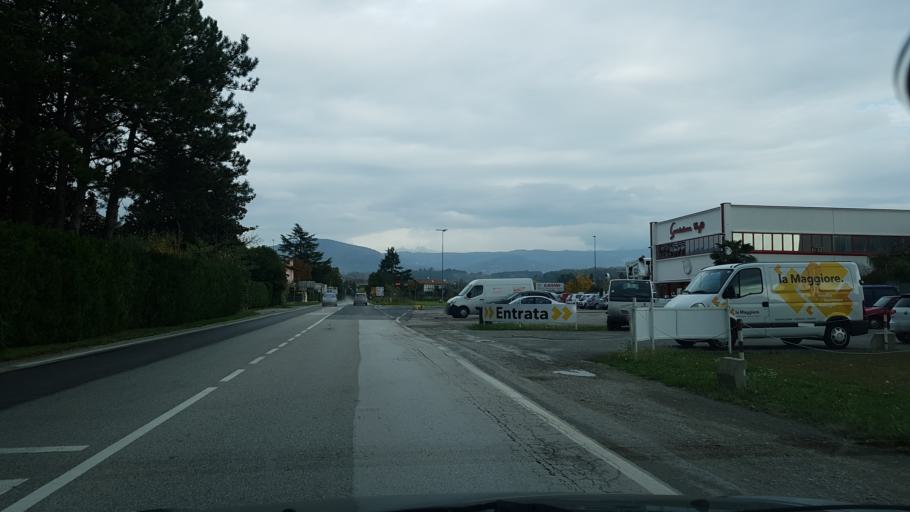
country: IT
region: Friuli Venezia Giulia
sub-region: Provincia di Gorizia
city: Gorizia
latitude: 45.9297
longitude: 13.6235
